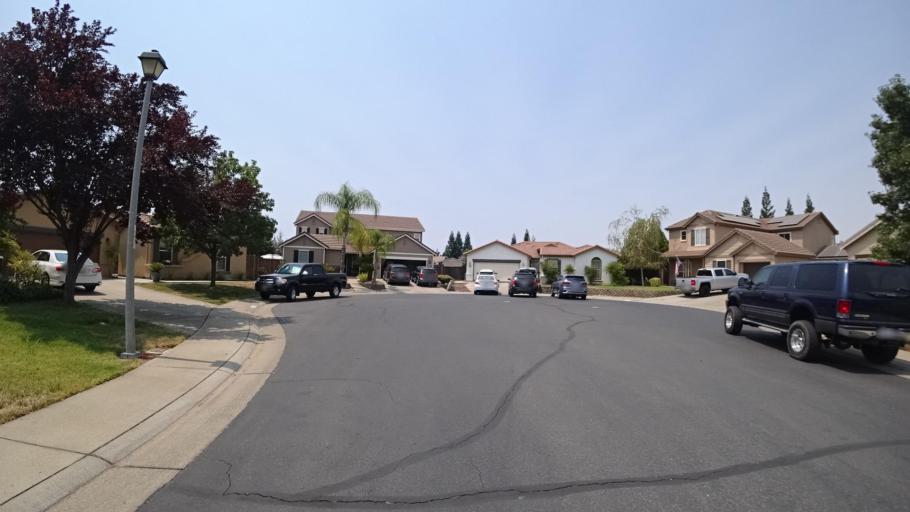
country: US
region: California
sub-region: Placer County
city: Roseville
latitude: 38.7990
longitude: -121.2835
